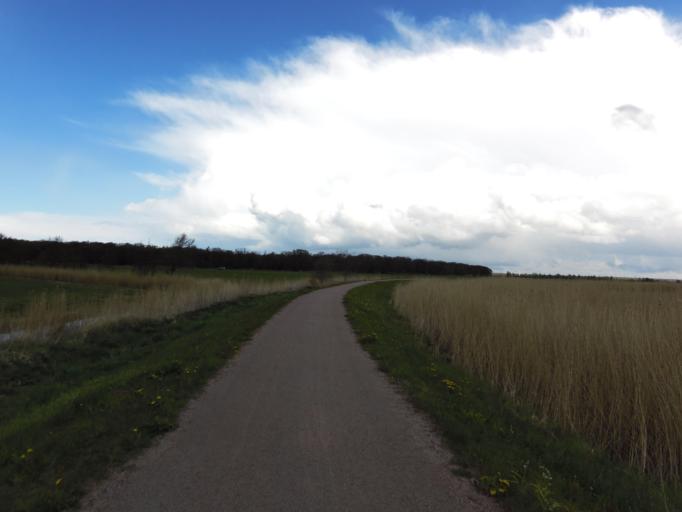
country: DE
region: Mecklenburg-Vorpommern
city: Saal
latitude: 54.3788
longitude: 12.4347
